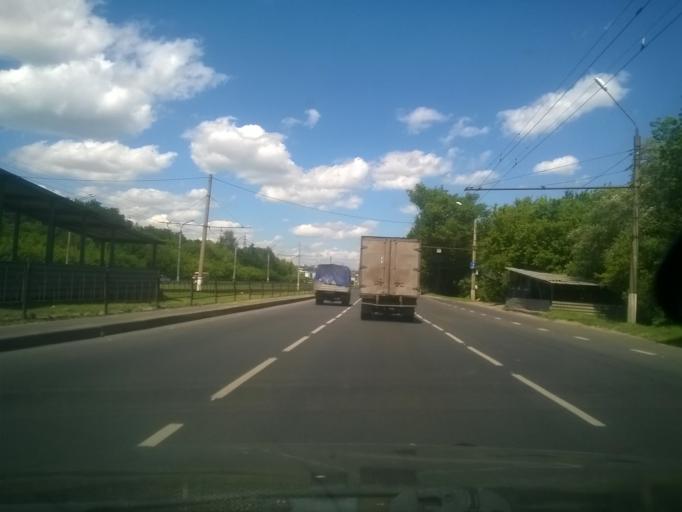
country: RU
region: Kursk
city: Kursk
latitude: 51.6818
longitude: 36.1497
